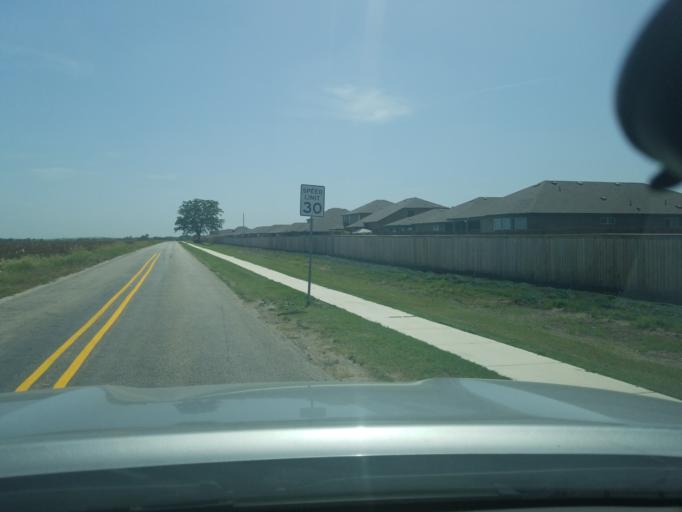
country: US
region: Texas
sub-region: Guadalupe County
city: Lake Dunlap
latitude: 29.6731
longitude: -98.0317
